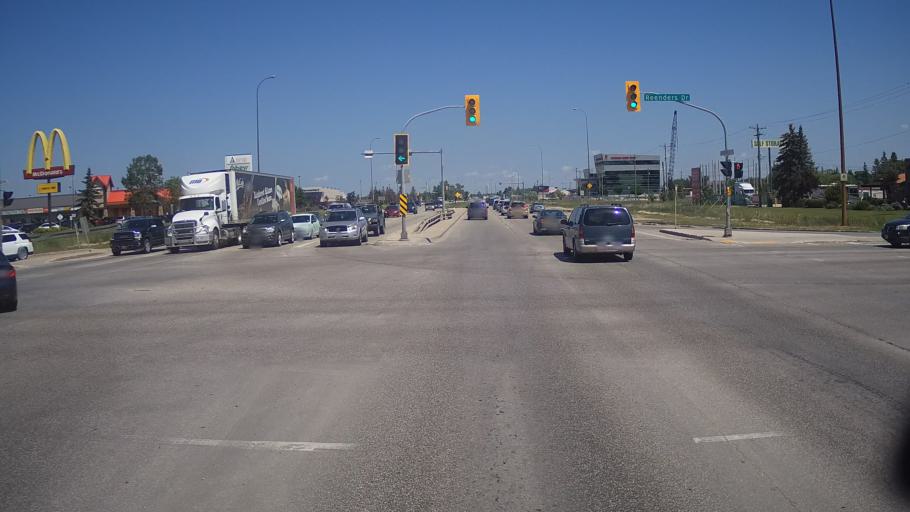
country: CA
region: Manitoba
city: Winnipeg
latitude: 49.9024
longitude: -97.0665
